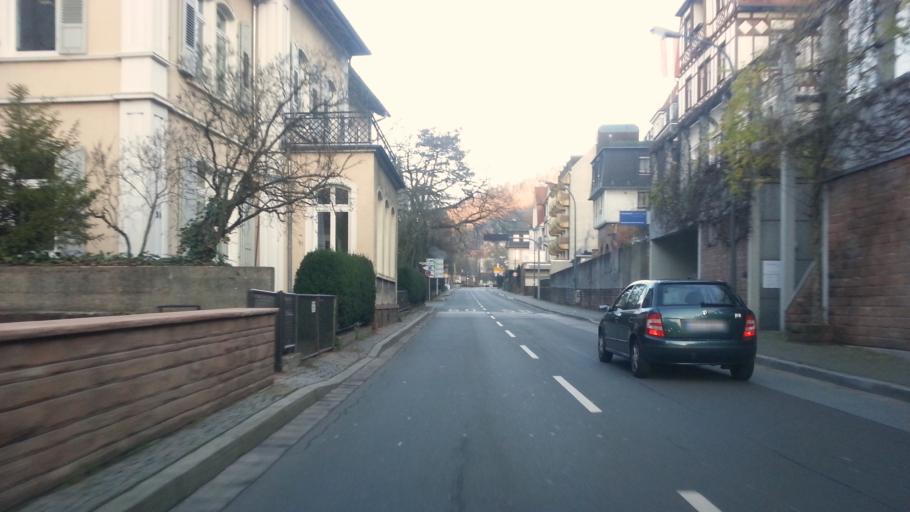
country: DE
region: Baden-Wuerttemberg
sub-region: Karlsruhe Region
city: Heidelberg
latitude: 49.4085
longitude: 8.7017
